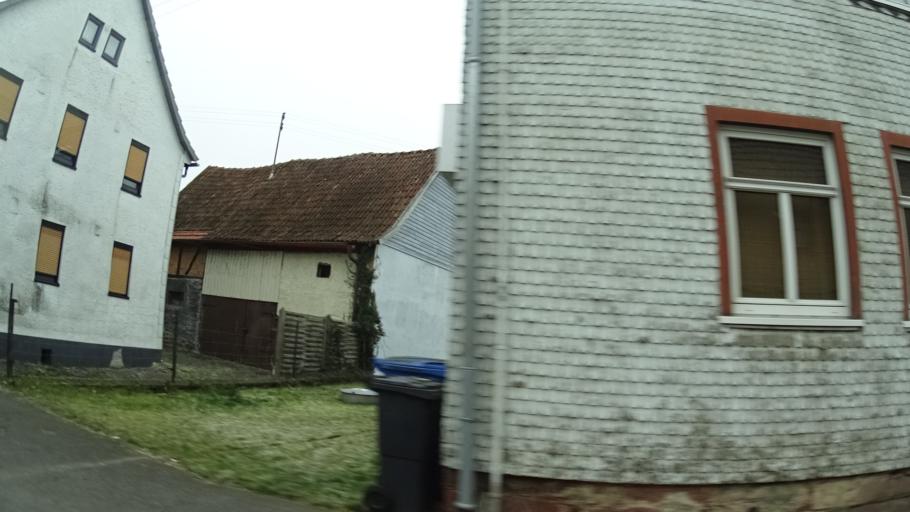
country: DE
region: Bavaria
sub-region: Regierungsbezirk Unterfranken
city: Zeitlofs
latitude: 50.2611
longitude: 9.6721
